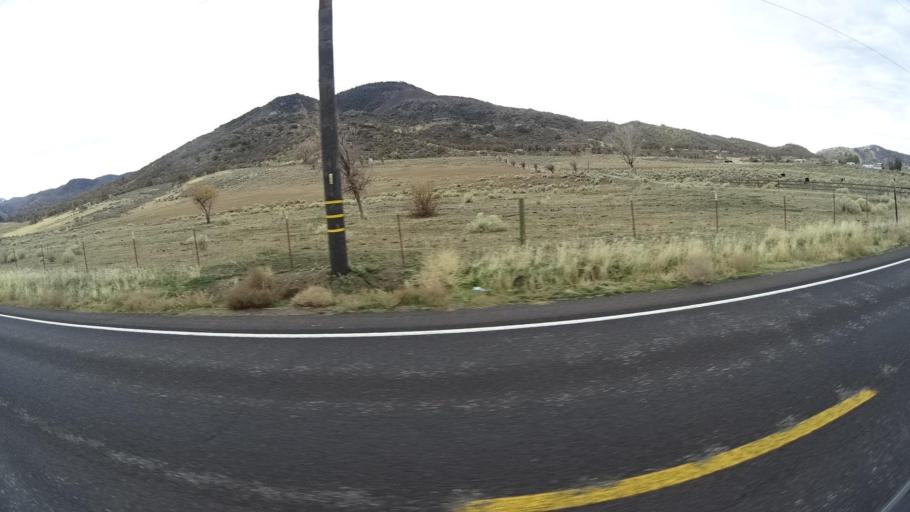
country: US
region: California
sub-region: Kern County
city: Stallion Springs
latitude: 35.0950
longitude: -118.5952
